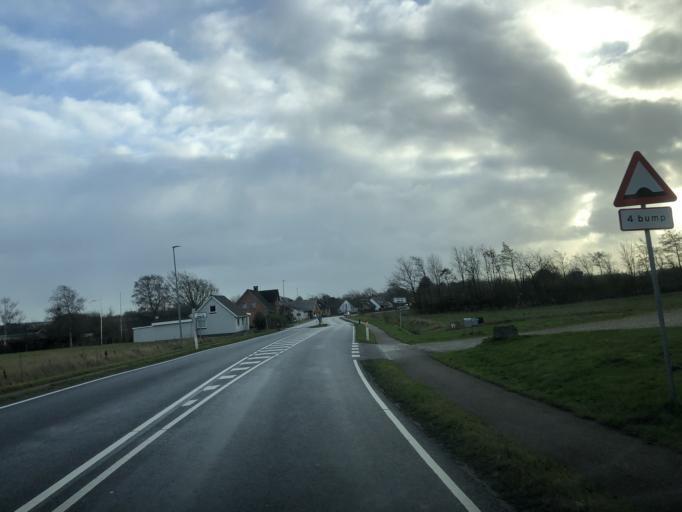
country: DK
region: North Denmark
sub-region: Rebild Kommune
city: Stovring
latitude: 56.8939
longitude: 9.7815
